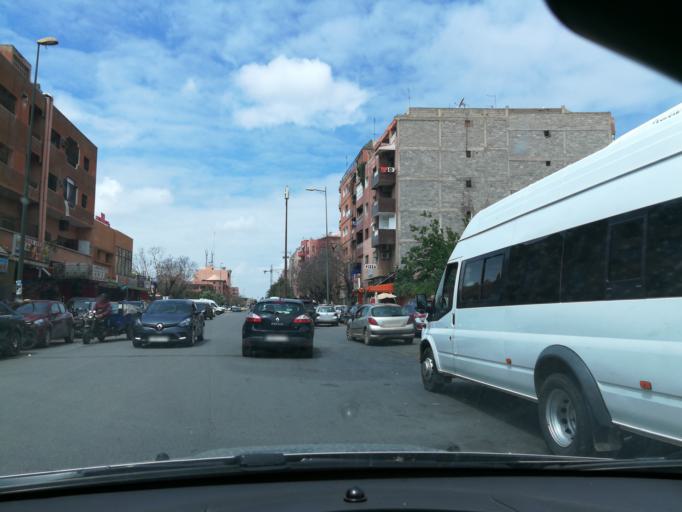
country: MA
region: Marrakech-Tensift-Al Haouz
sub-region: Marrakech
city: Marrakesh
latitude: 31.6326
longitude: -8.0117
